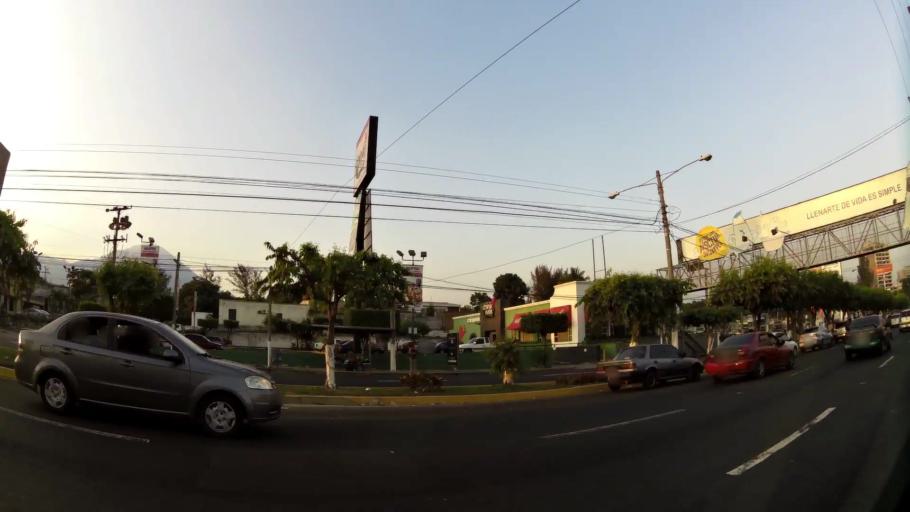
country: SV
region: San Salvador
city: San Salvador
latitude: 13.7089
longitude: -89.2100
